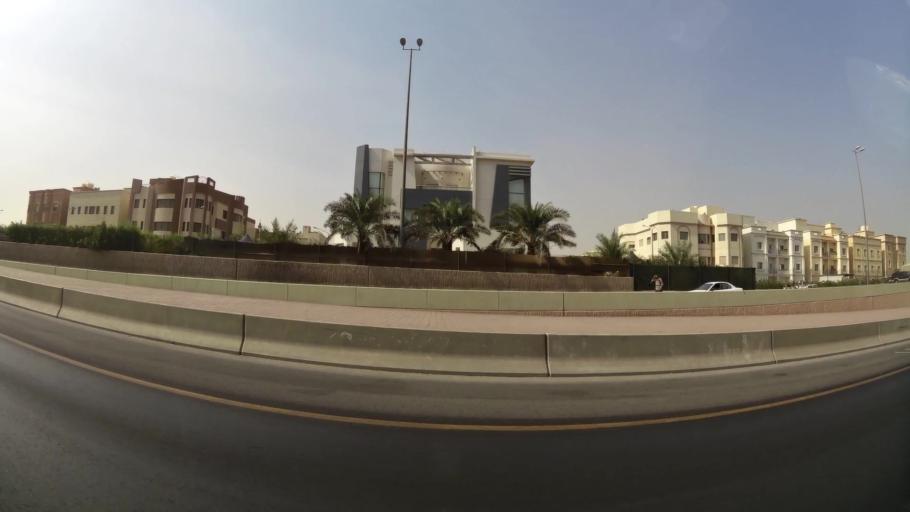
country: KW
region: Al Farwaniyah
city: Al Farwaniyah
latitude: 29.2760
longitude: 47.9501
